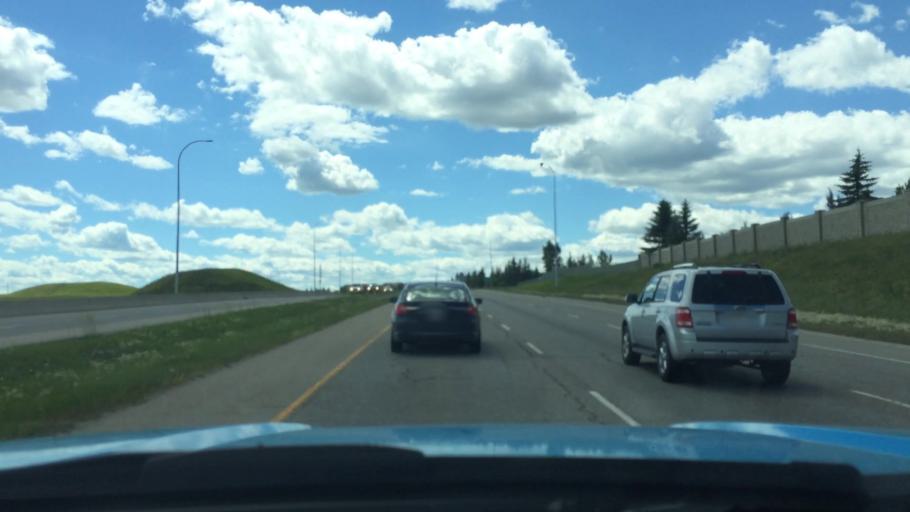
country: CA
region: Alberta
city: Calgary
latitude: 51.1313
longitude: -114.1267
